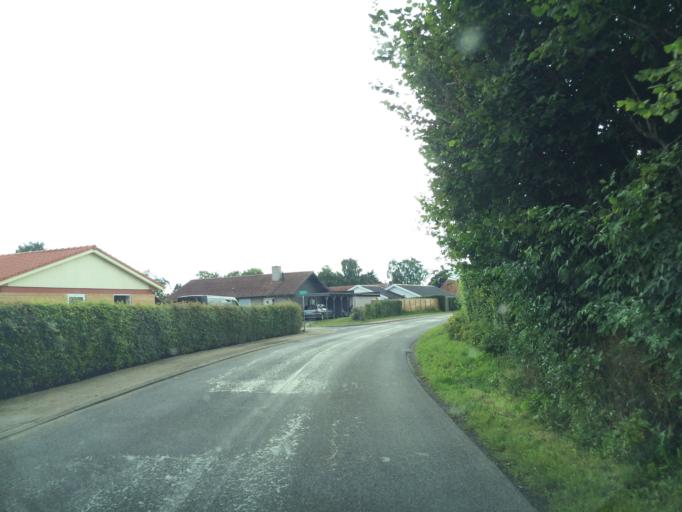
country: DK
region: South Denmark
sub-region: Odense Kommune
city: Bellinge
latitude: 55.2728
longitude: 10.3164
